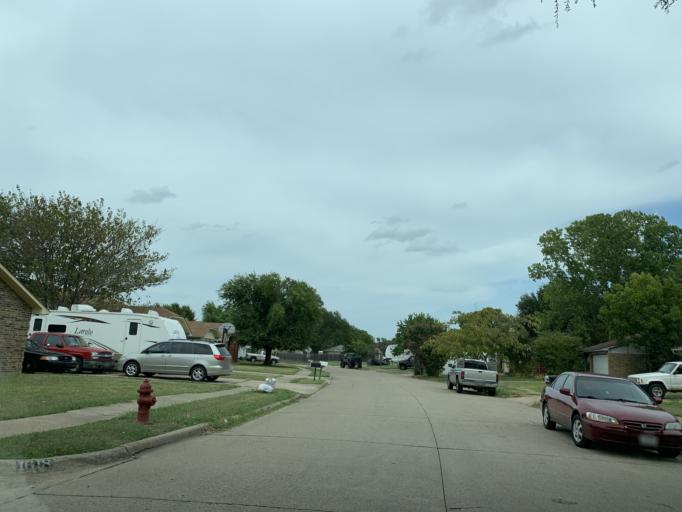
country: US
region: Texas
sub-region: Dallas County
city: Cedar Hill
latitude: 32.6515
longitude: -97.0262
